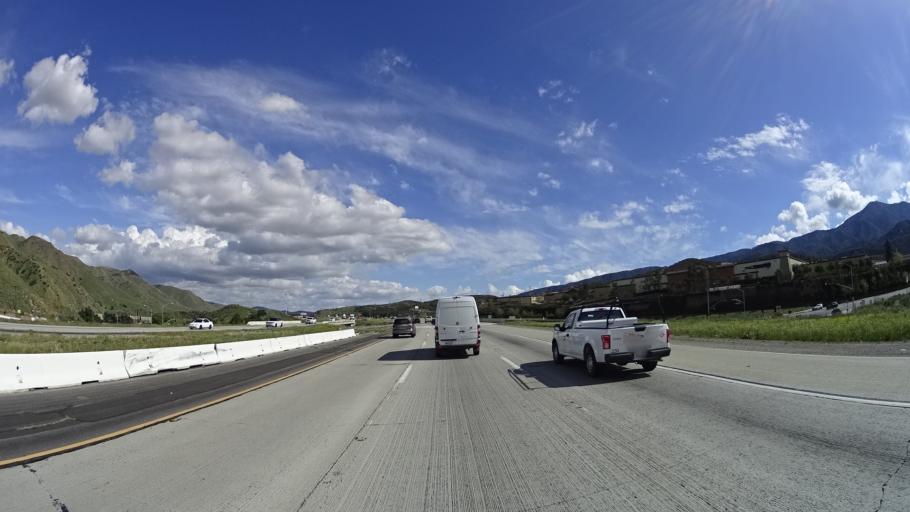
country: US
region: California
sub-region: Riverside County
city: El Cerrito
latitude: 33.7494
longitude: -117.4535
